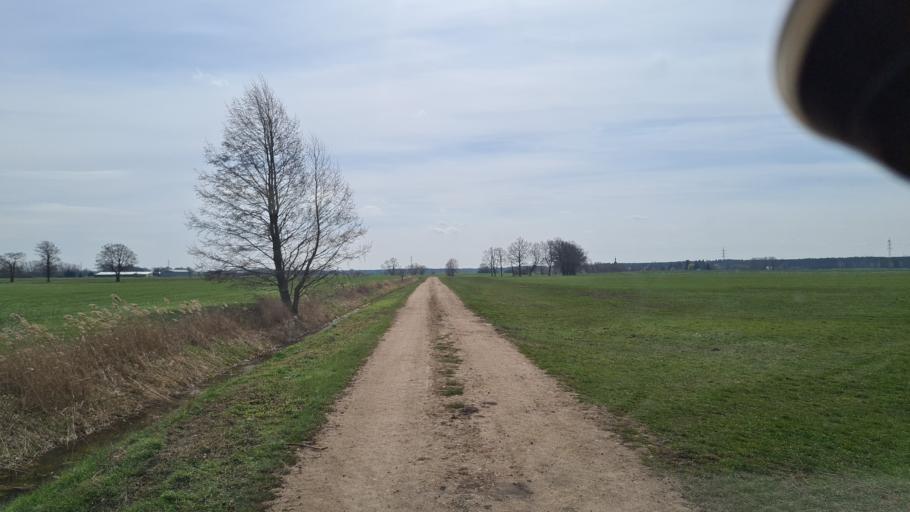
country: DE
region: Brandenburg
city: Bronkow
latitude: 51.6064
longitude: 13.9274
